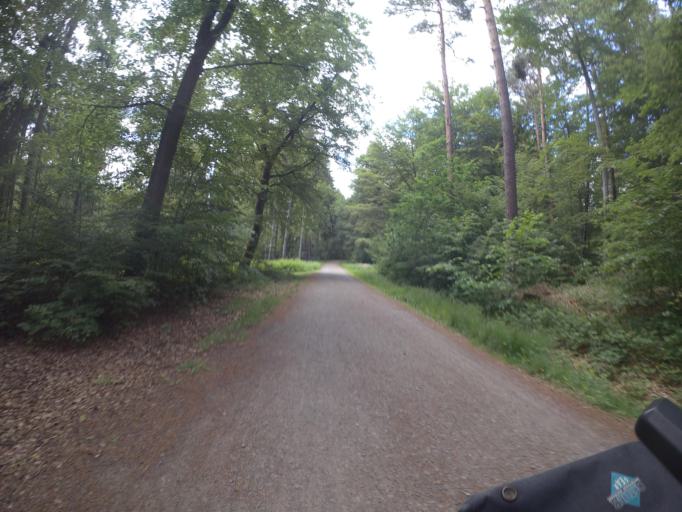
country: DE
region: Rheinland-Pfalz
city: Otterbach
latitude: 49.4477
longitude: 7.7195
